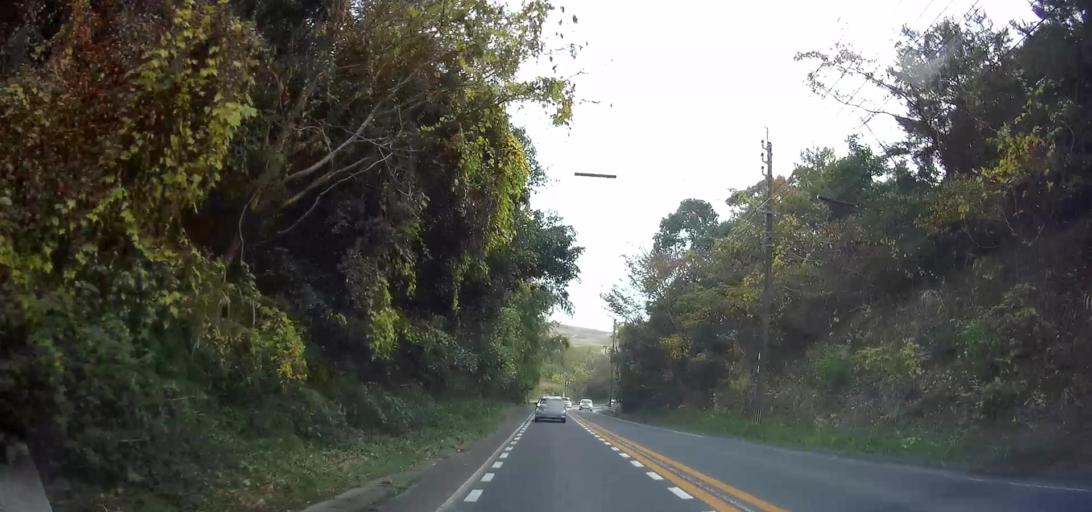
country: JP
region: Nagasaki
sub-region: Isahaya-shi
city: Isahaya
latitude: 32.7899
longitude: 130.0537
